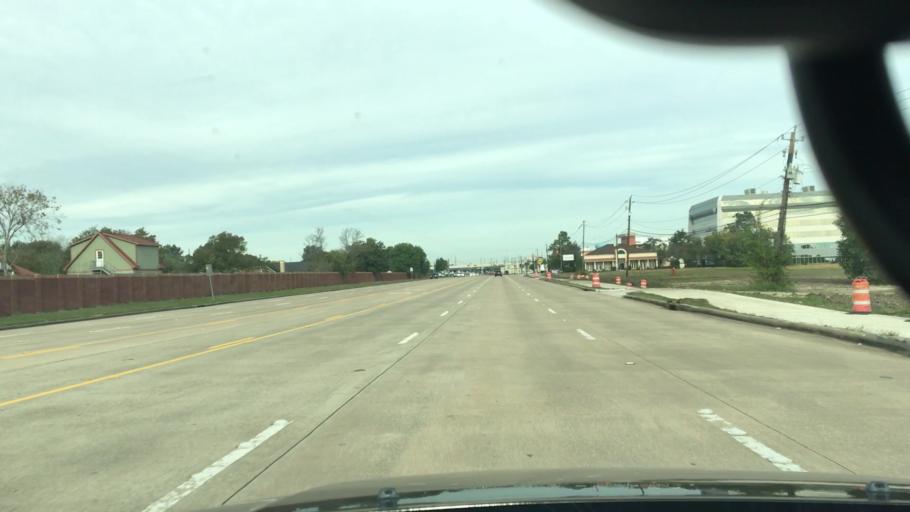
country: US
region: Texas
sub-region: Harris County
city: Nassau Bay
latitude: 29.5406
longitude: -95.1012
